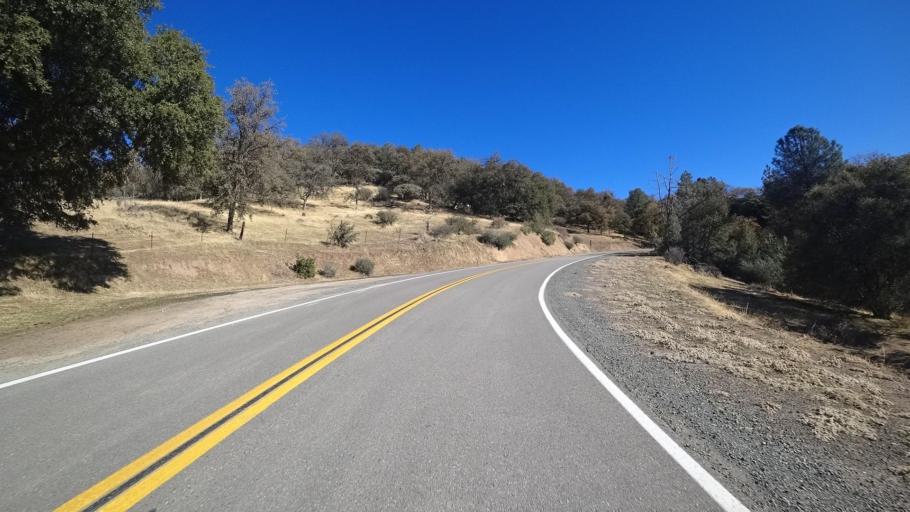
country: US
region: California
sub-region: Kern County
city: Alta Sierra
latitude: 35.7374
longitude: -118.6183
